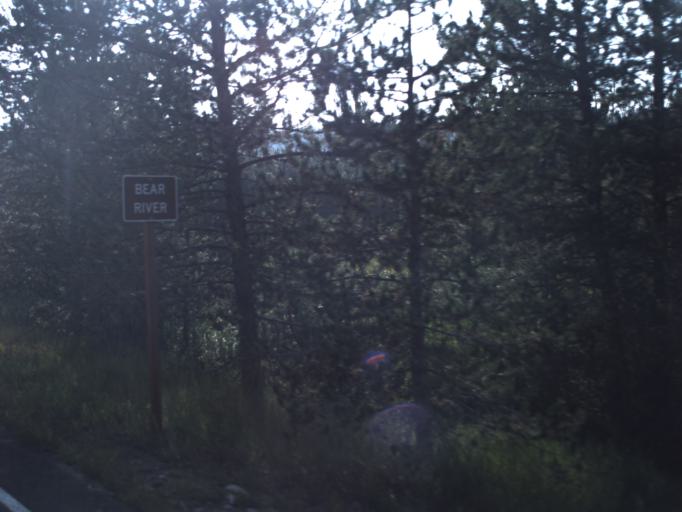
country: US
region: Wyoming
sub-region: Uinta County
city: Evanston
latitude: 40.8723
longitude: -110.8341
